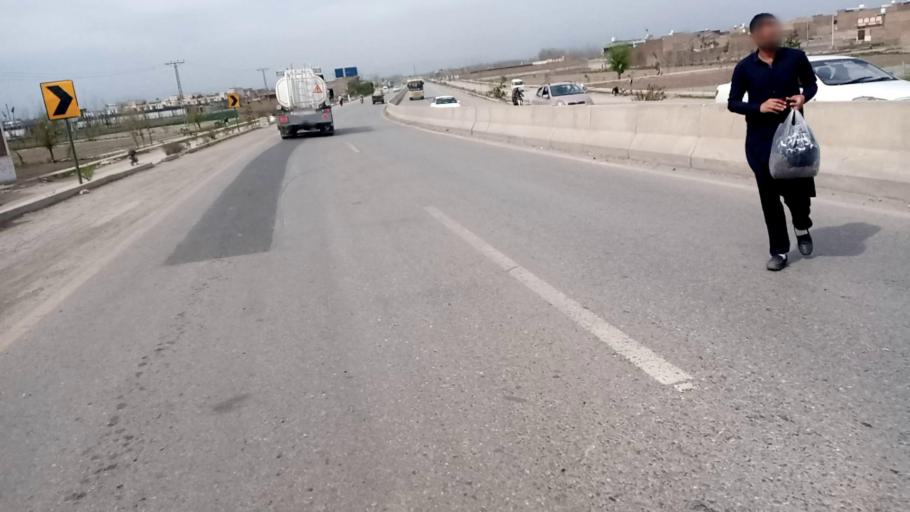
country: PK
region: Khyber Pakhtunkhwa
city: Peshawar
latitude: 34.0401
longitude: 71.6189
